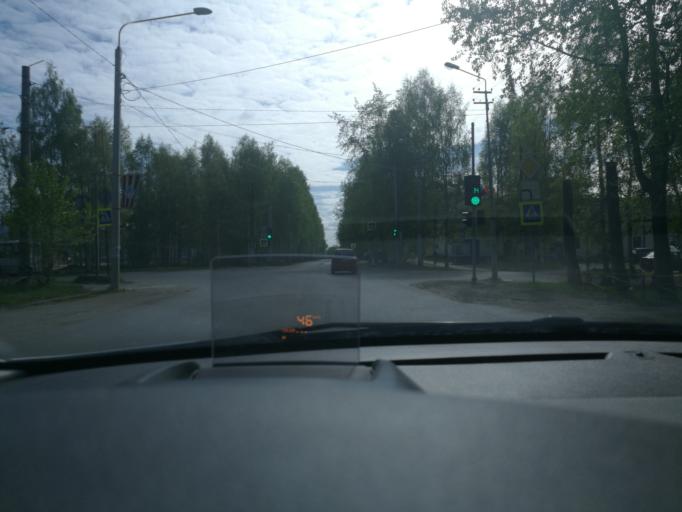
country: RU
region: Arkhangelskaya
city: Arkhangel'sk
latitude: 64.5927
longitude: 40.5891
